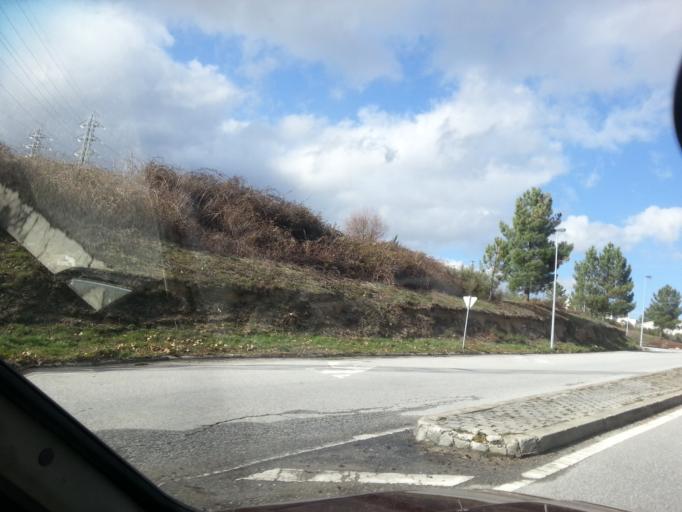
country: PT
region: Guarda
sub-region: Guarda
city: Guarda
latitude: 40.5361
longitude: -7.2879
